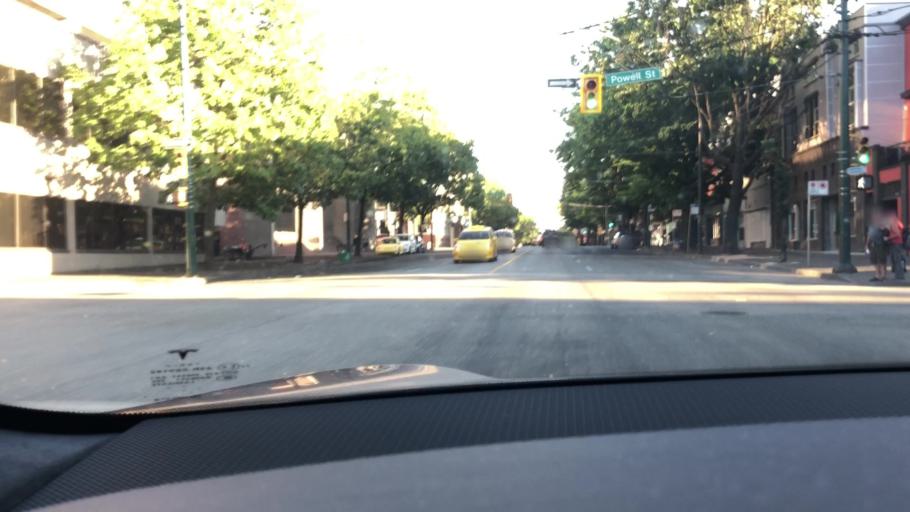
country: CA
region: British Columbia
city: West End
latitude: 49.2832
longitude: -123.0996
